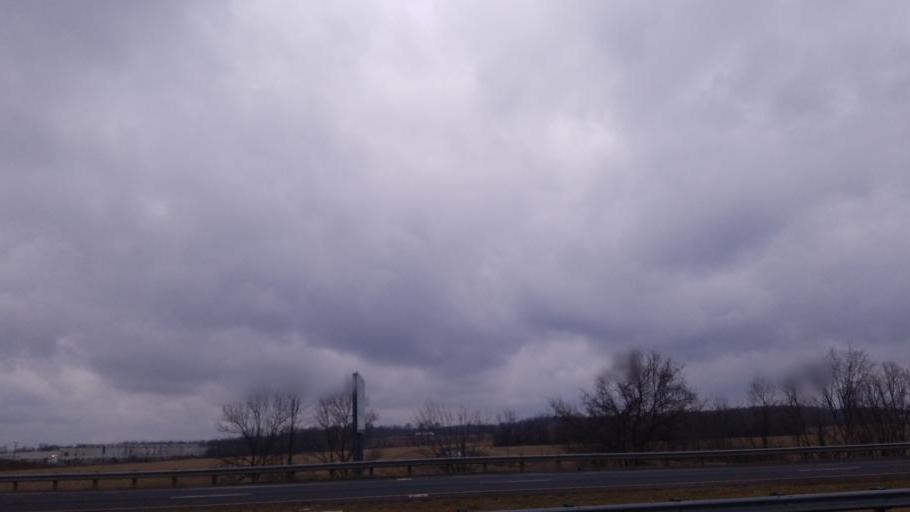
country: US
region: Ohio
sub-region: Knox County
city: Fredericktown
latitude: 40.4822
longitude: -82.5589
